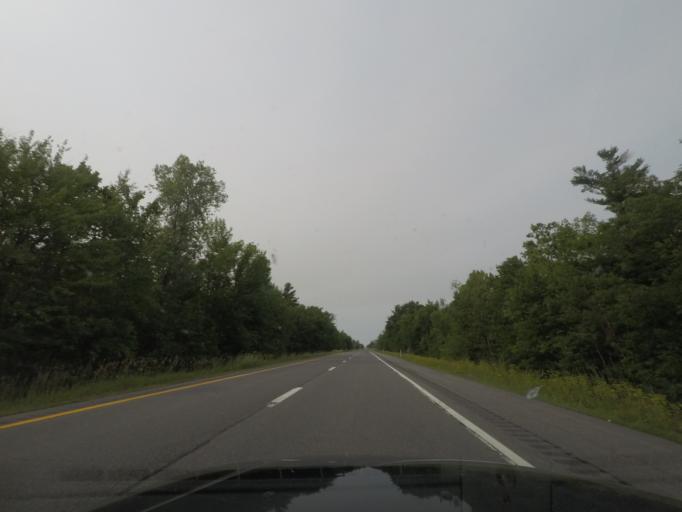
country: US
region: New York
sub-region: Clinton County
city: Champlain
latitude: 44.9342
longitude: -73.4465
